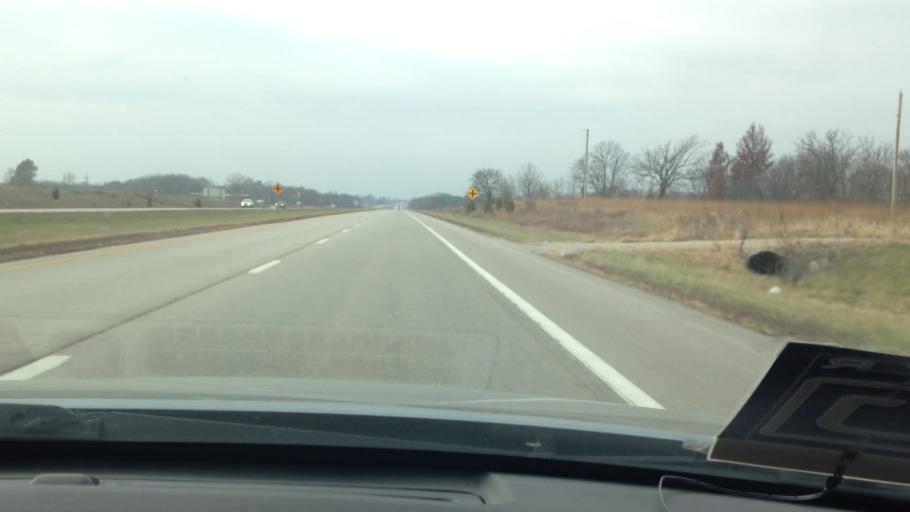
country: US
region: Missouri
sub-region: Cass County
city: Garden City
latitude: 38.5769
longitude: -94.2049
